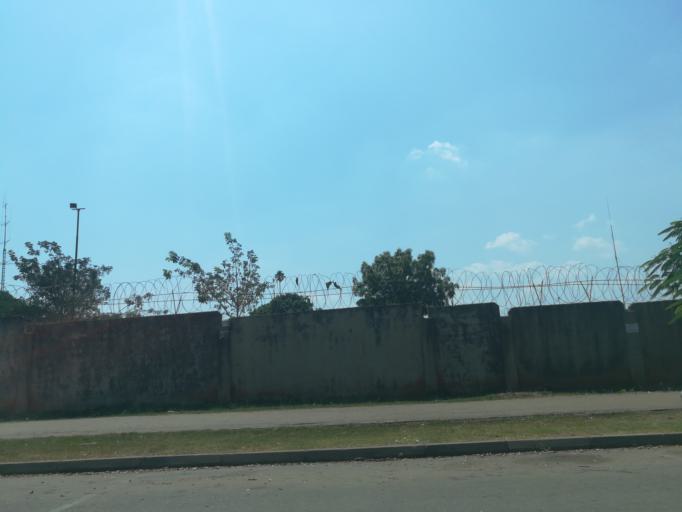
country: NG
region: Abuja Federal Capital Territory
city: Abuja
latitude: 9.0644
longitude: 7.4494
